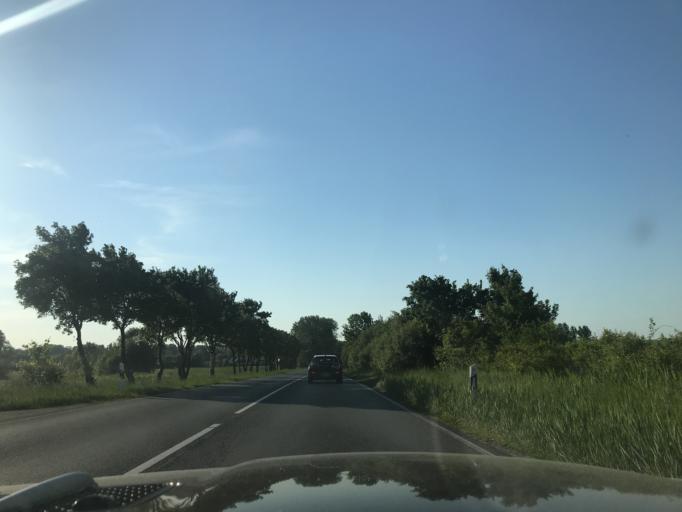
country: DE
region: Thuringia
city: Hohenkirchen
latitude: 50.8437
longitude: 10.7129
